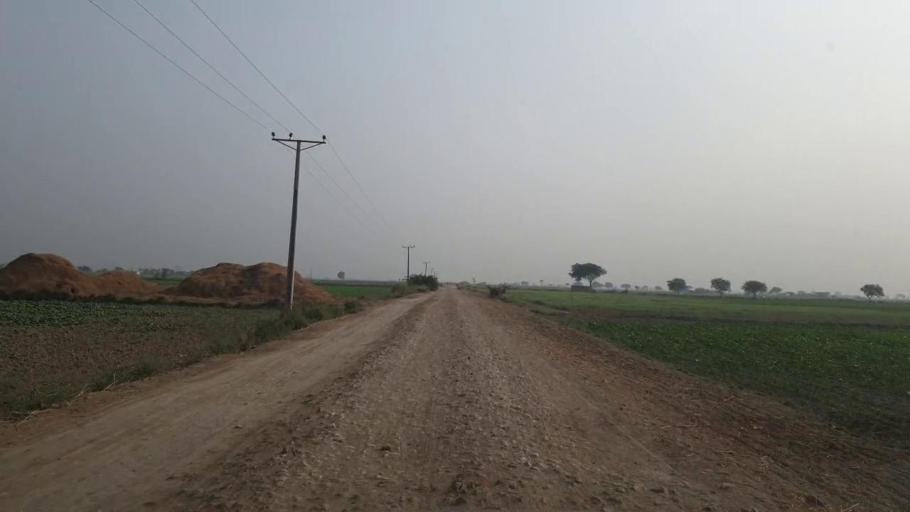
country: PK
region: Sindh
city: Mirpur Batoro
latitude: 24.5637
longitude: 68.4187
